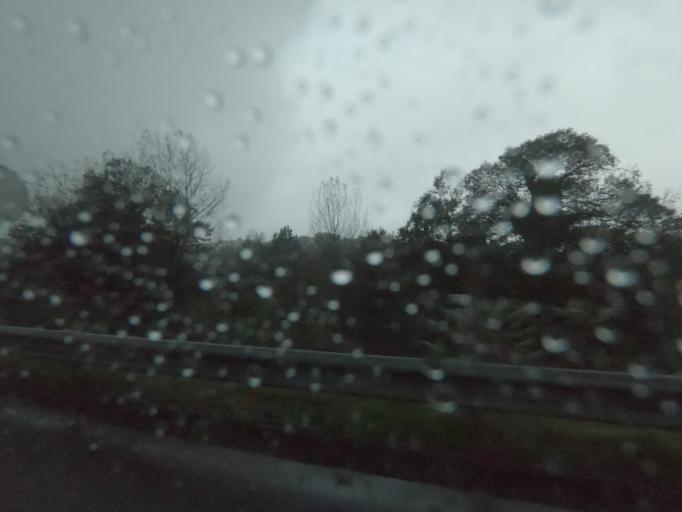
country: PT
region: Braga
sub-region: Braga
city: Braga
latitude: 41.5321
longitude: -8.4454
